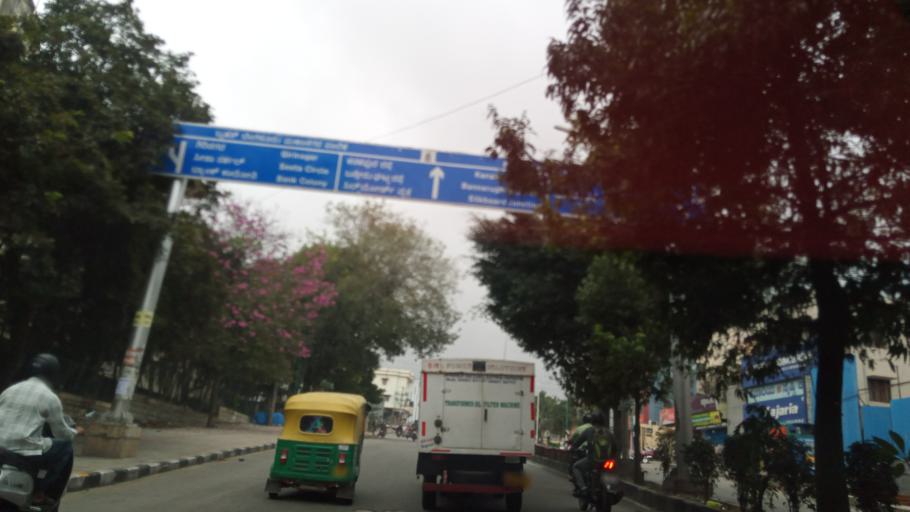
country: IN
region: Karnataka
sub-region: Bangalore Urban
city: Bangalore
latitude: 12.9318
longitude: 77.5419
